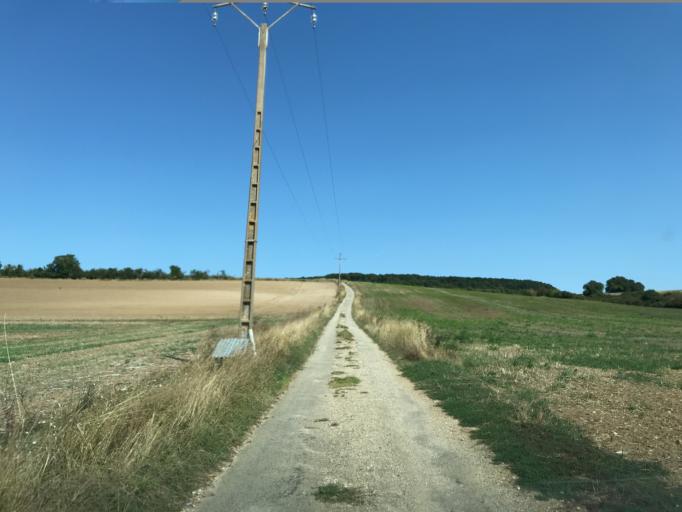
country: FR
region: Haute-Normandie
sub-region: Departement de l'Eure
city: Heudreville-sur-Eure
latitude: 49.1240
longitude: 1.2233
